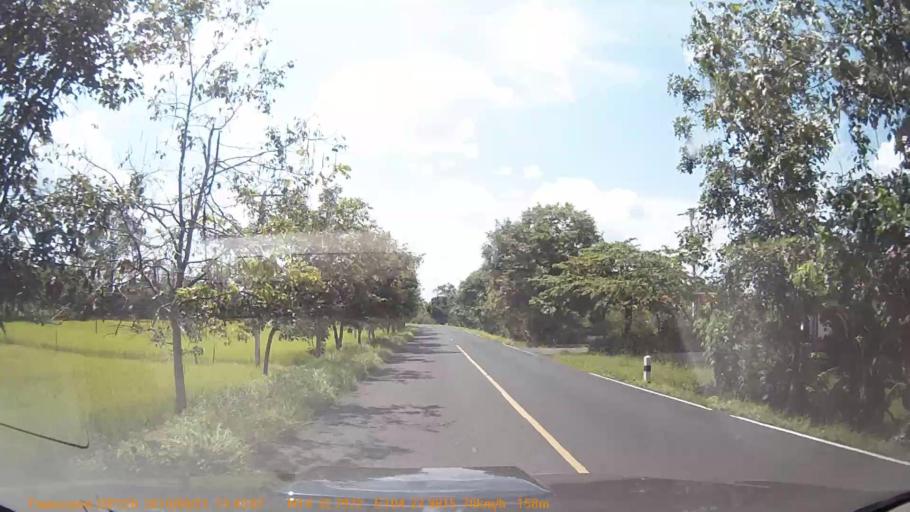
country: TH
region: Sisaket
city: Khun Han
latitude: 14.5468
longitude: 104.4659
